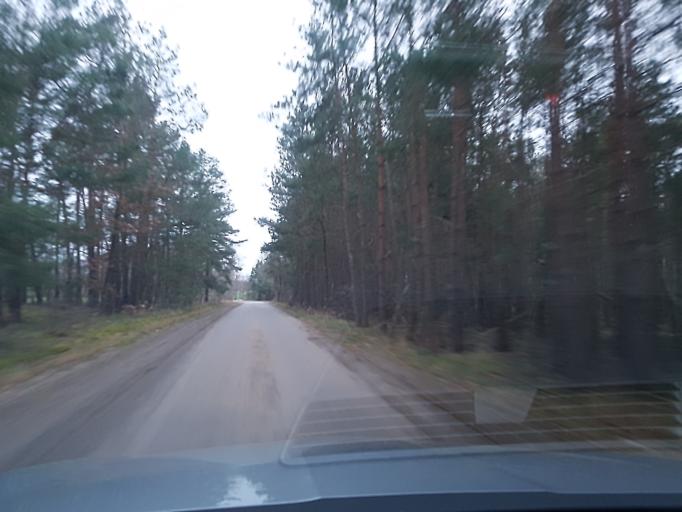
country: DE
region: Brandenburg
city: Schonewalde
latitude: 51.6448
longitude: 13.6134
